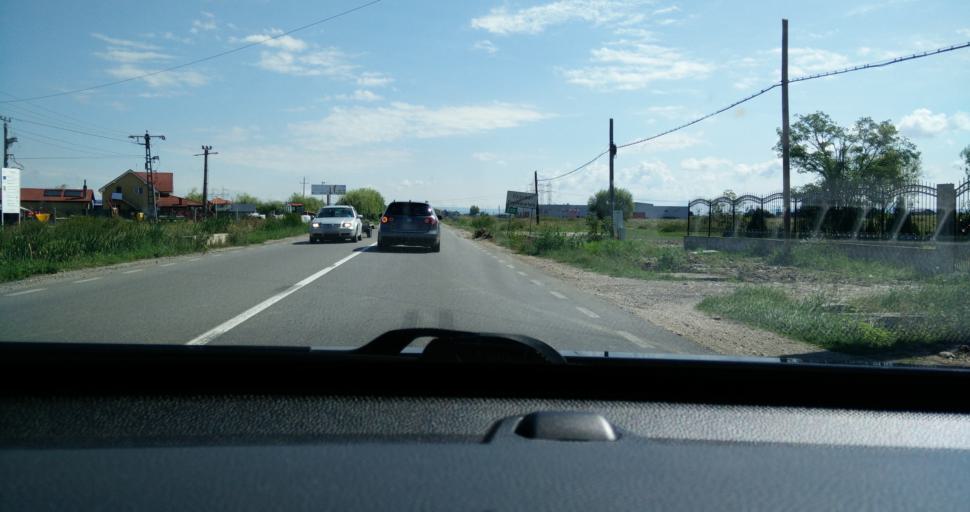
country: RO
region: Bihor
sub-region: Comuna Osorheiu
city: Osorheiu
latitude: 47.0493
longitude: 22.0469
